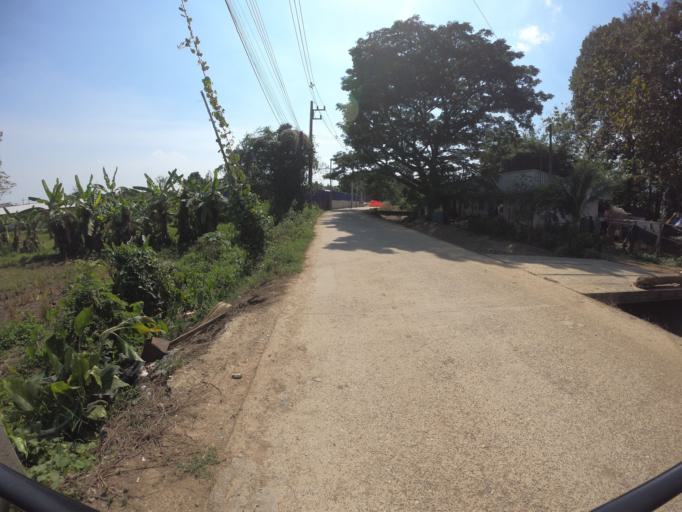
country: TH
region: Chiang Mai
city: San Sai
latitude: 18.8670
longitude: 98.9840
